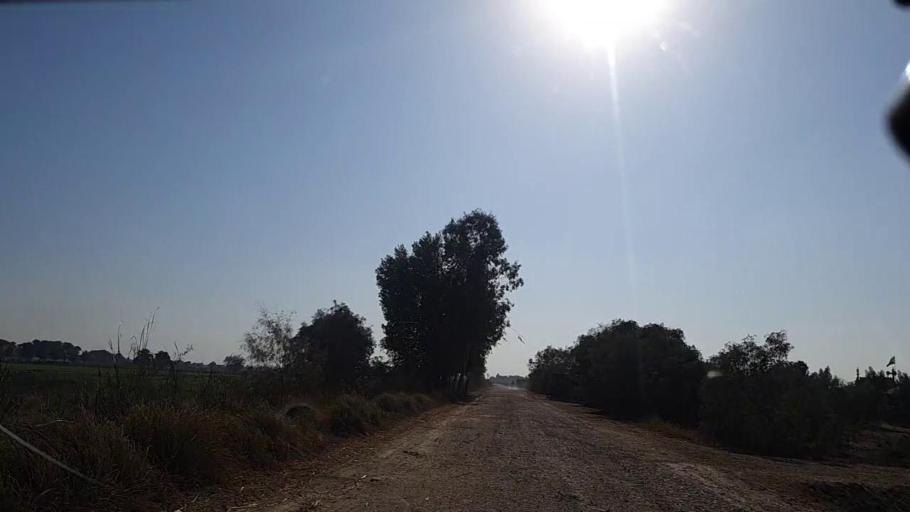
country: PK
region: Sindh
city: Khanpur
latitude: 27.7975
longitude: 69.3734
